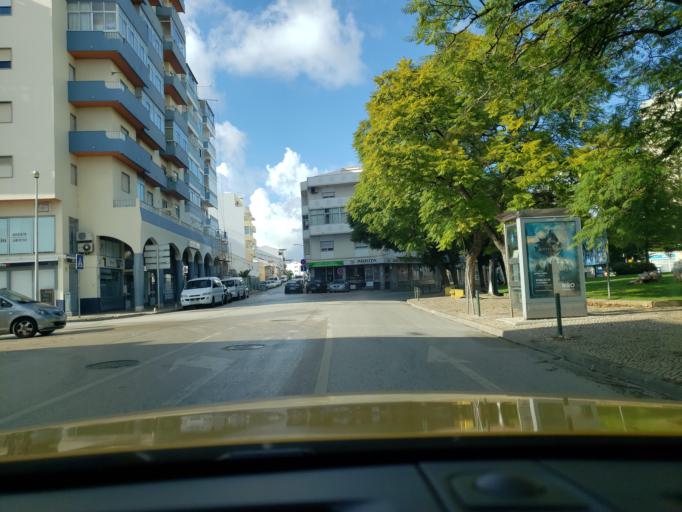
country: PT
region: Faro
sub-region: Portimao
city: Portimao
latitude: 37.1439
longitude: -8.5401
